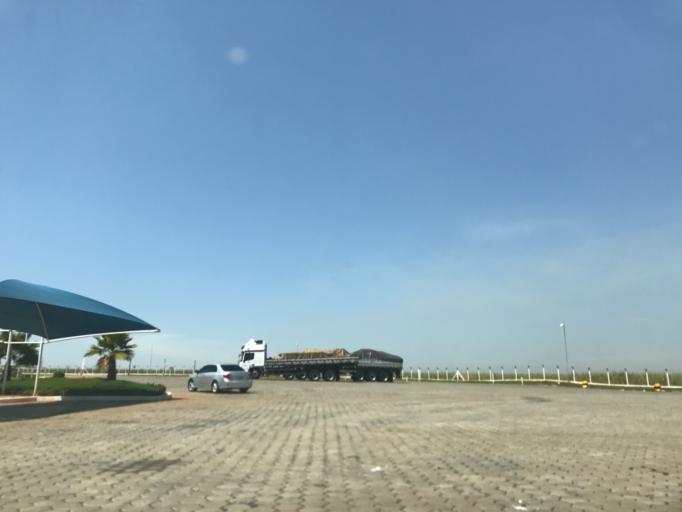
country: BR
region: Sao Paulo
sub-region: Nova Granada
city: Nova Granada
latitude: -20.4487
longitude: -49.2825
